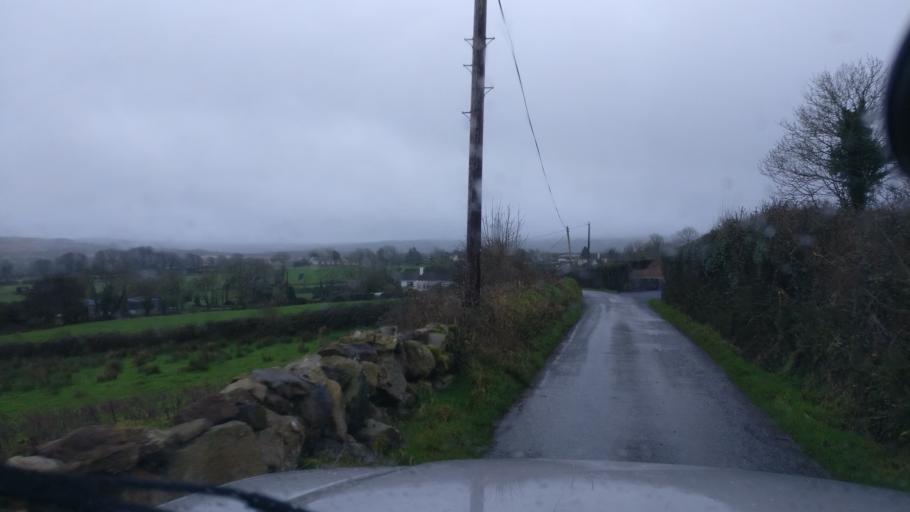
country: IE
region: Connaught
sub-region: County Galway
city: Loughrea
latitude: 53.1656
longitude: -8.6416
